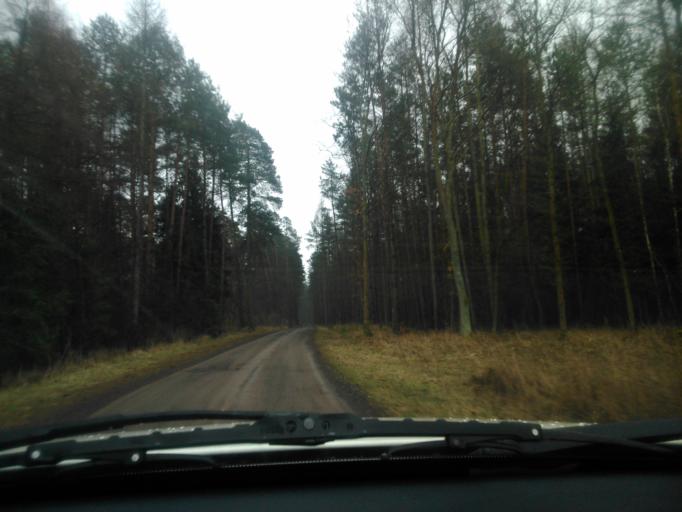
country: PL
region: Kujawsko-Pomorskie
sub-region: Powiat golubsko-dobrzynski
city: Radomin
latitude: 53.1589
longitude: 19.1491
